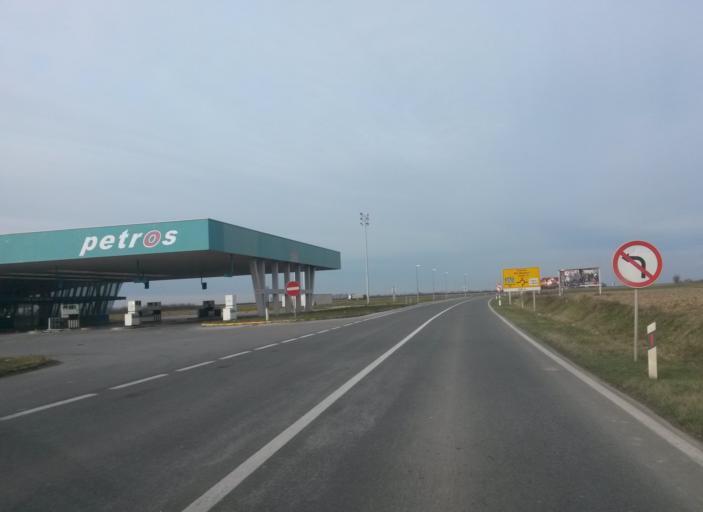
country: HR
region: Osjecko-Baranjska
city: Cepin
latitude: 45.5124
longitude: 18.5383
